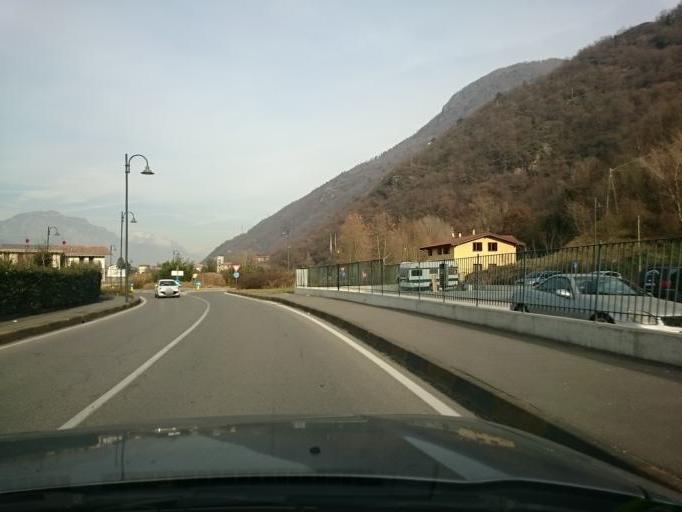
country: IT
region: Lombardy
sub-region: Provincia di Brescia
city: Pisogne
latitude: 45.8110
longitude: 10.1126
